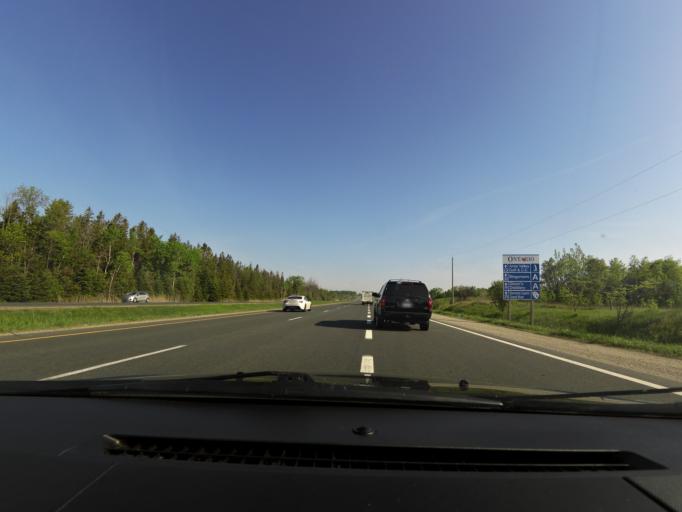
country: CA
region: Ontario
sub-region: Wellington County
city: Guelph
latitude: 43.4522
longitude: -80.1783
